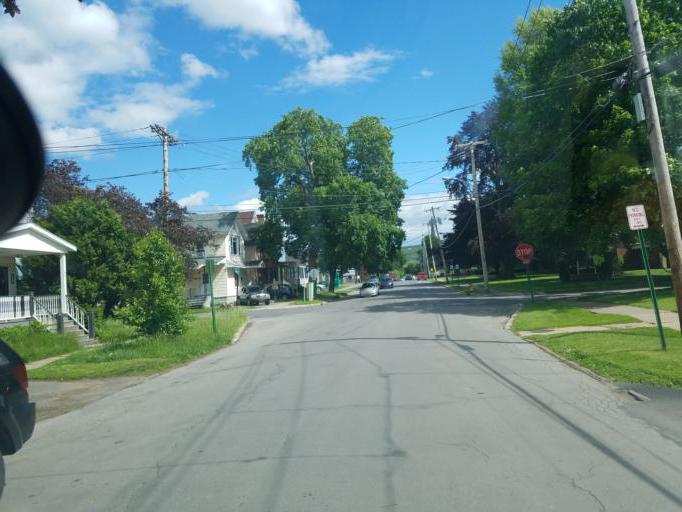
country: US
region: New York
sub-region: Herkimer County
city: Herkimer
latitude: 43.0285
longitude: -74.9911
